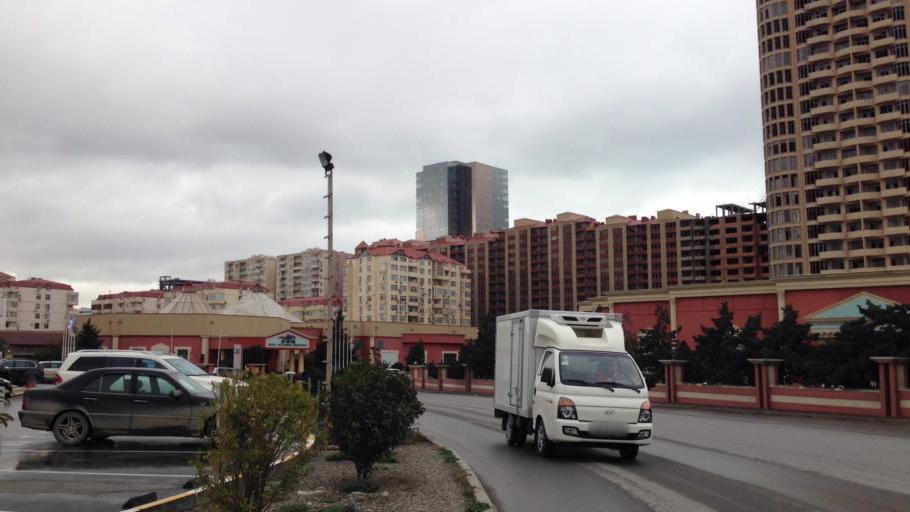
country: AZ
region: Baki
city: Baku
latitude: 40.3859
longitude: 49.8670
